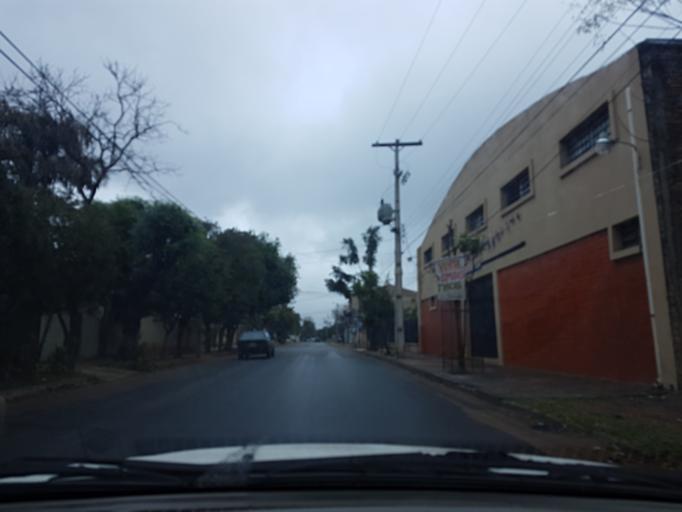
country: PY
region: Central
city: San Lorenzo
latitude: -25.2693
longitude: -57.4797
